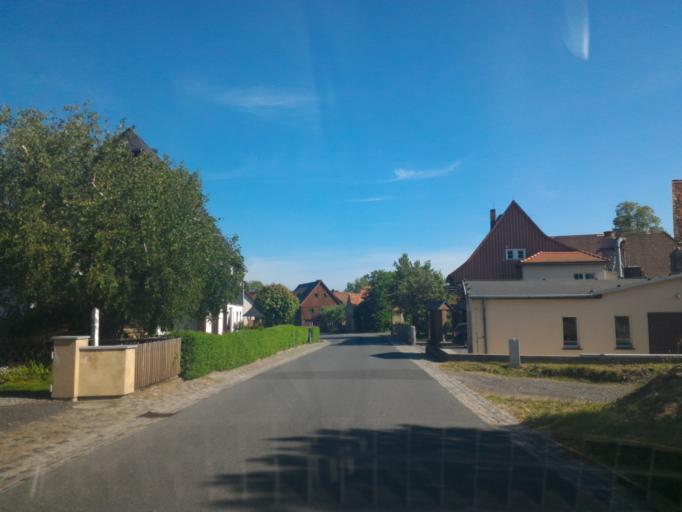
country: DE
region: Saxony
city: Niedercunnersdorf
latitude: 51.0241
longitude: 14.6766
